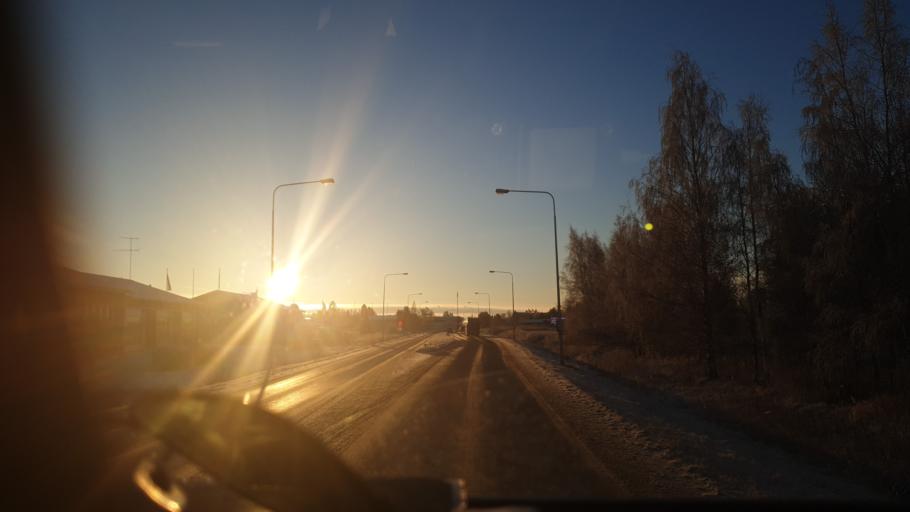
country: FI
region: Northern Ostrobothnia
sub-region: Ylivieska
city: Kalajoki
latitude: 64.2667
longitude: 23.9492
